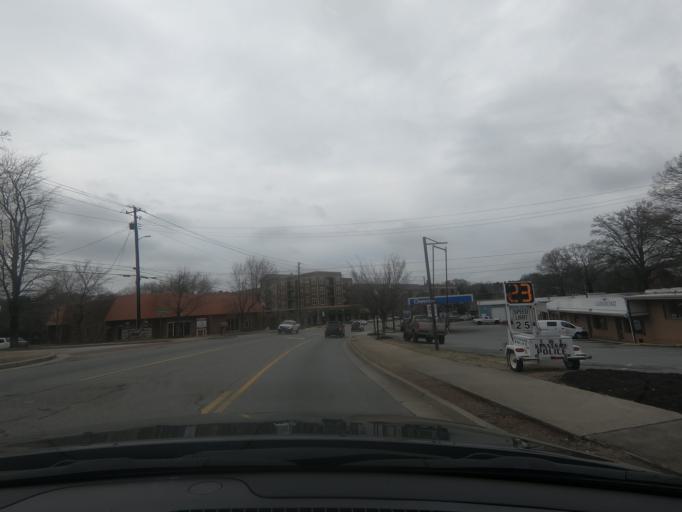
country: US
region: Georgia
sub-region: Cobb County
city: Kennesaw
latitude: 34.0209
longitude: -84.6145
